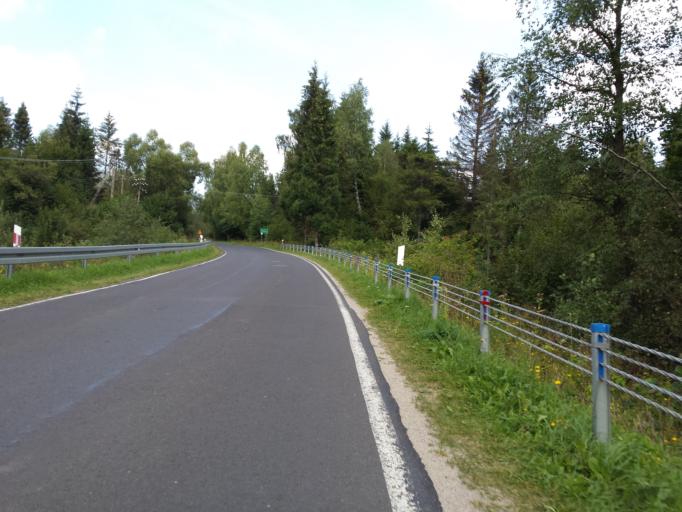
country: PL
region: Subcarpathian Voivodeship
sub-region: Powiat leski
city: Cisna
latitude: 49.1844
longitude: 22.4283
